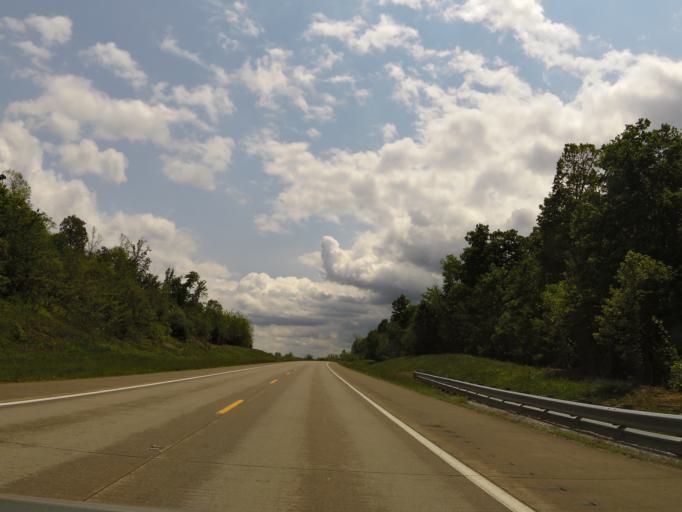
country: US
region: West Virginia
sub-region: Mason County
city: New Haven
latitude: 39.0143
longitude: -81.9138
